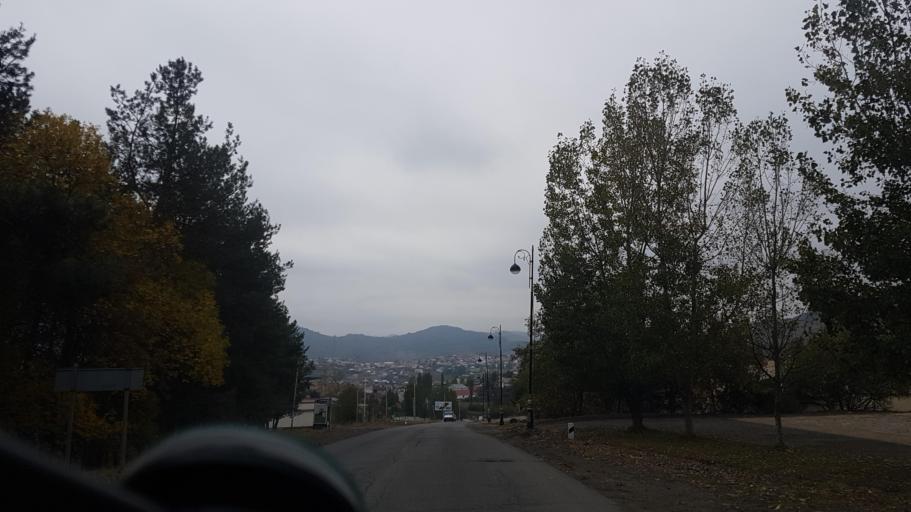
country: AZ
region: Gadabay Rayon
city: Ariqdam
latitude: 40.5991
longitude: 45.8106
